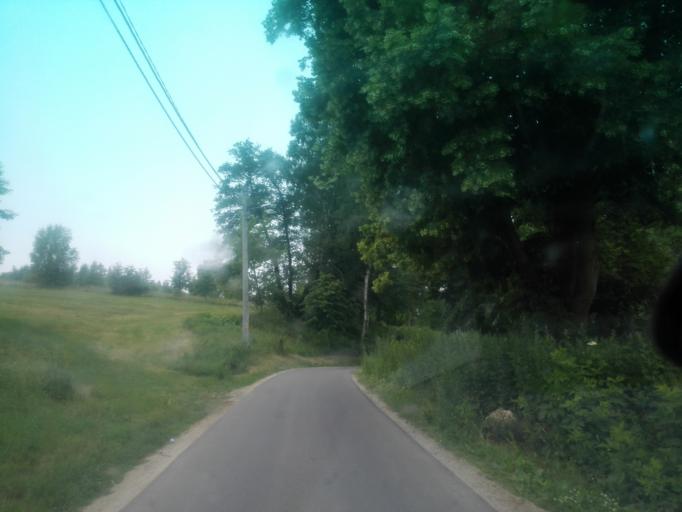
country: PL
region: Silesian Voivodeship
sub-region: Powiat czestochowski
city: Mstow
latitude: 50.8259
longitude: 19.3069
